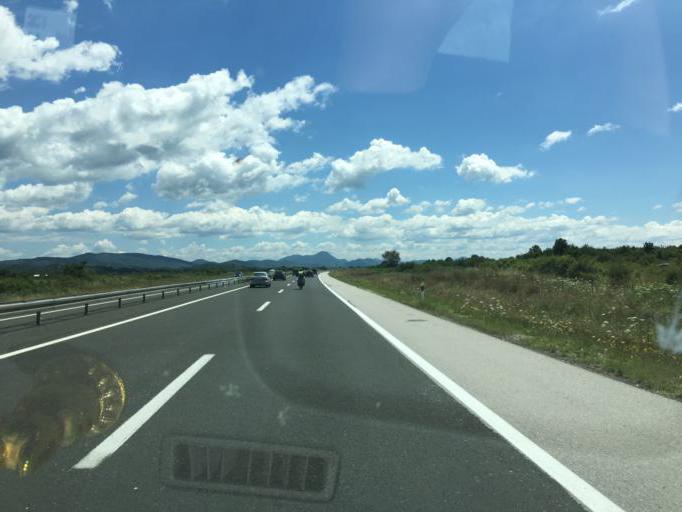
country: HR
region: Licko-Senjska
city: Gospic
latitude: 44.5131
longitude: 15.5089
